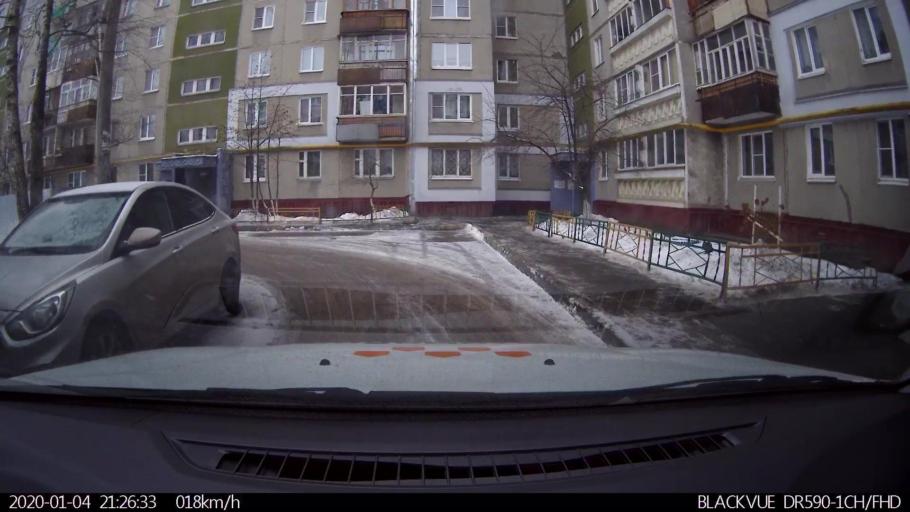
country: RU
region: Nizjnij Novgorod
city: Burevestnik
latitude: 56.2185
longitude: 43.8364
